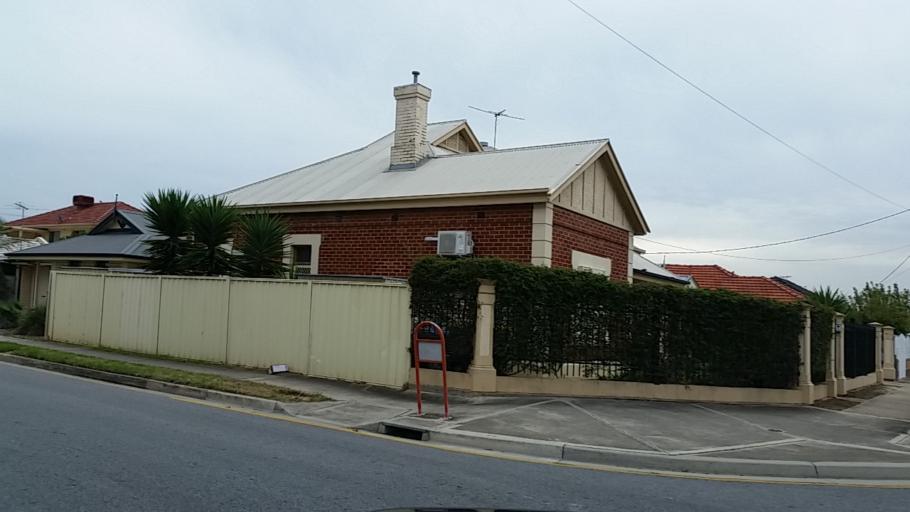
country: AU
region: South Australia
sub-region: Charles Sturt
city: Royal Park
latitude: -34.8759
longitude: 138.5116
